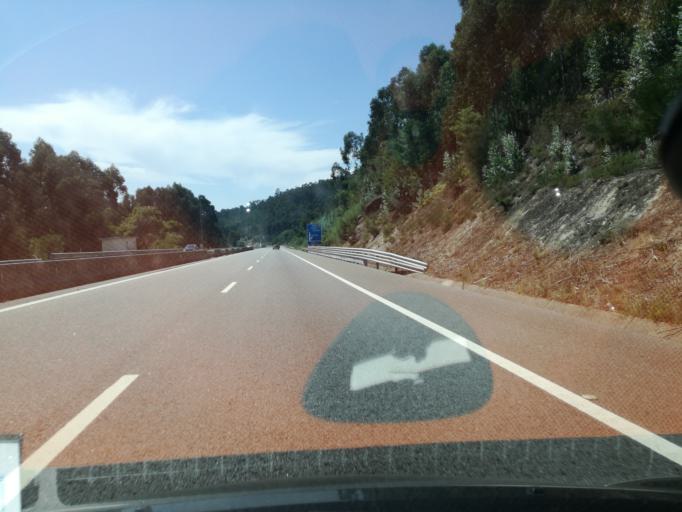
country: PT
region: Viana do Castelo
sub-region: Viana do Castelo
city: Meadela
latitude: 41.7535
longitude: -8.7976
